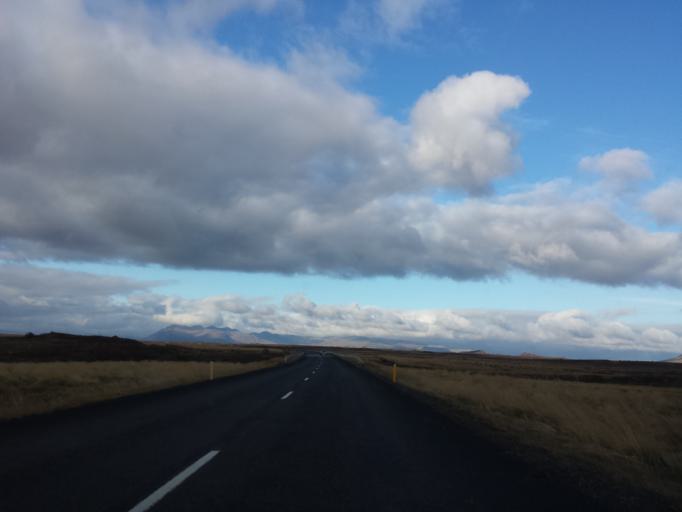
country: IS
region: West
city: Borgarnes
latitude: 64.7312
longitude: -22.1824
